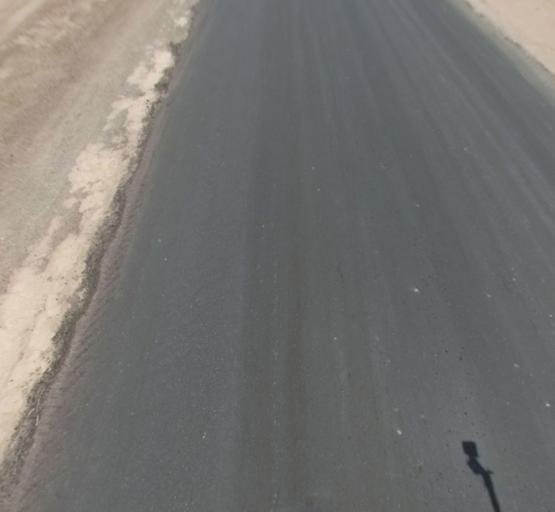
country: US
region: California
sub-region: Madera County
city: Chowchilla
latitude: 37.1049
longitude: -120.3826
